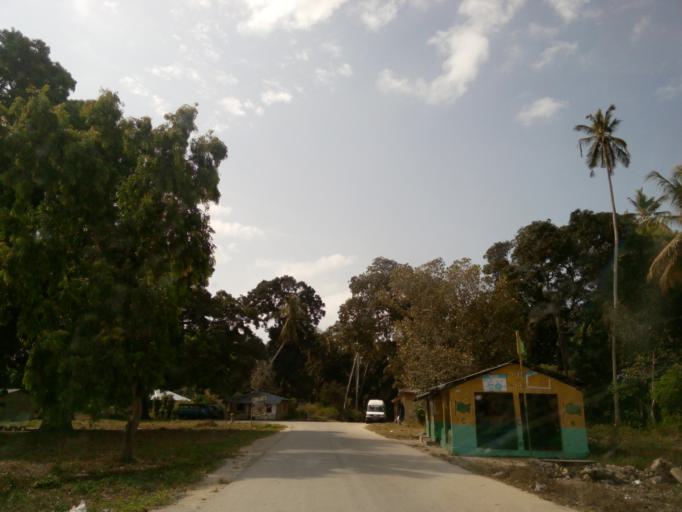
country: TZ
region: Zanzibar Central/South
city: Mahonda
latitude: -6.3084
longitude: 39.3748
